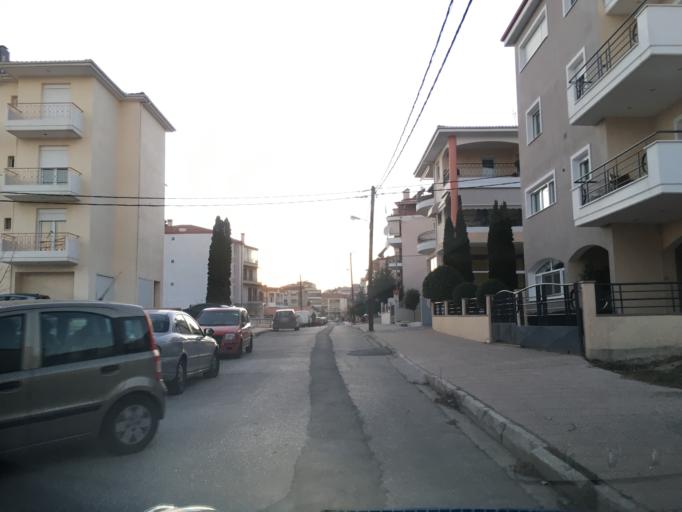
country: GR
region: West Macedonia
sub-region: Nomos Kozanis
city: Kozani
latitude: 40.3032
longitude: 21.8020
